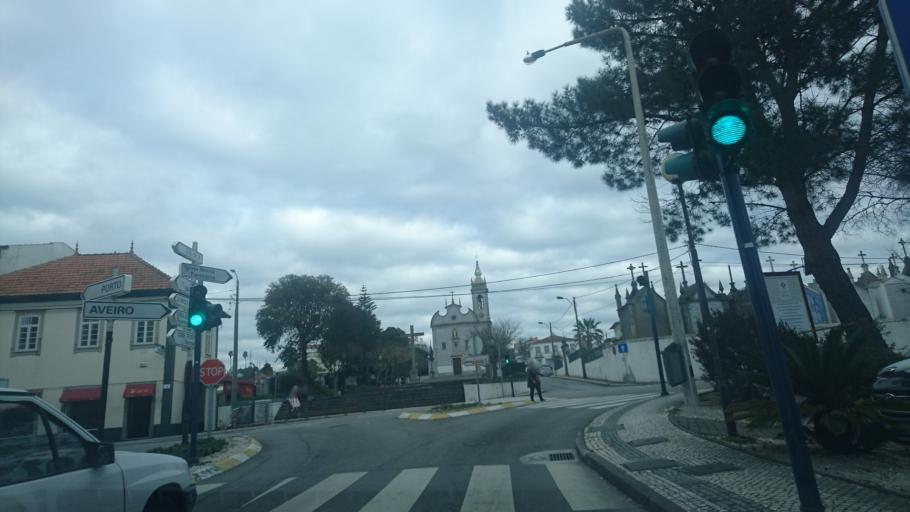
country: PT
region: Aveiro
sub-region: Ovar
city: Esmoriz
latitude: 40.9556
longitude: -8.6264
